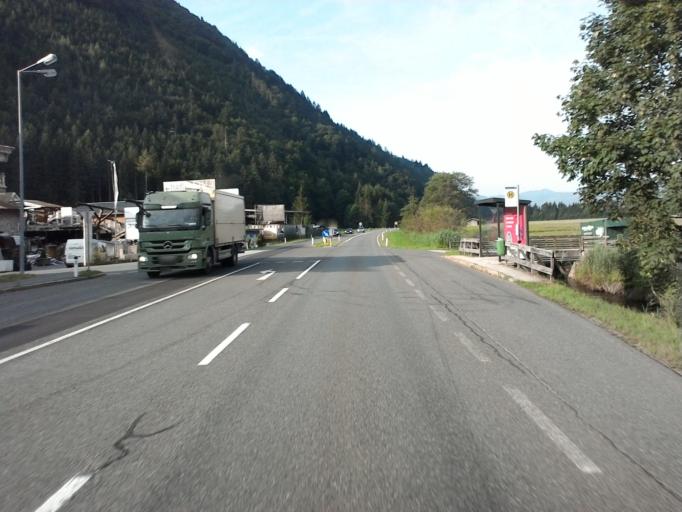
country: AT
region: Tyrol
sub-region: Politischer Bezirk Kitzbuhel
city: Kirchdorf in Tirol
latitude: 47.5665
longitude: 12.4673
